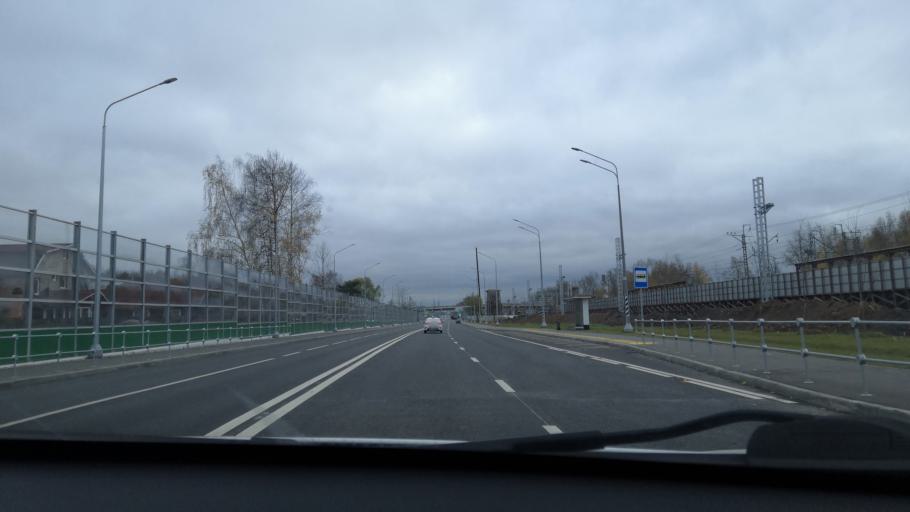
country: RU
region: Moscow
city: Severnyy
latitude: 55.9279
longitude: 37.5269
